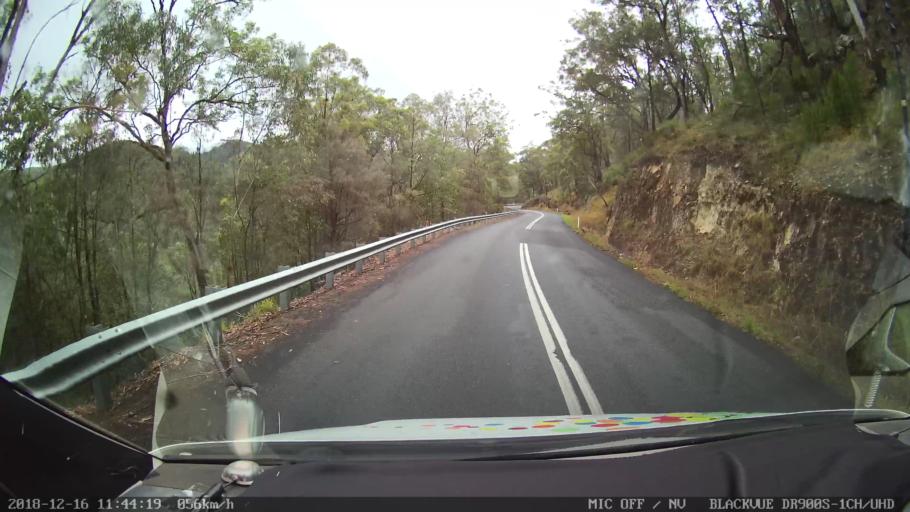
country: AU
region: New South Wales
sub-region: Tenterfield Municipality
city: Carrolls Creek
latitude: -28.9393
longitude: 152.2196
